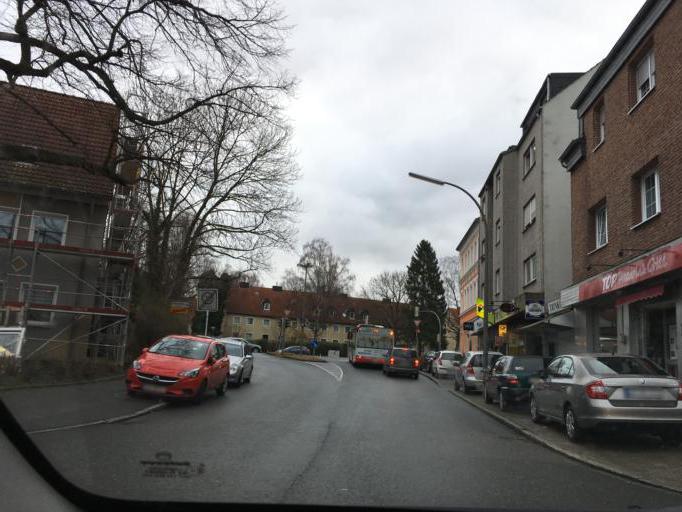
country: DE
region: North Rhine-Westphalia
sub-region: Regierungsbezirk Arnsberg
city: Dortmund
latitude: 51.4754
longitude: 7.4463
